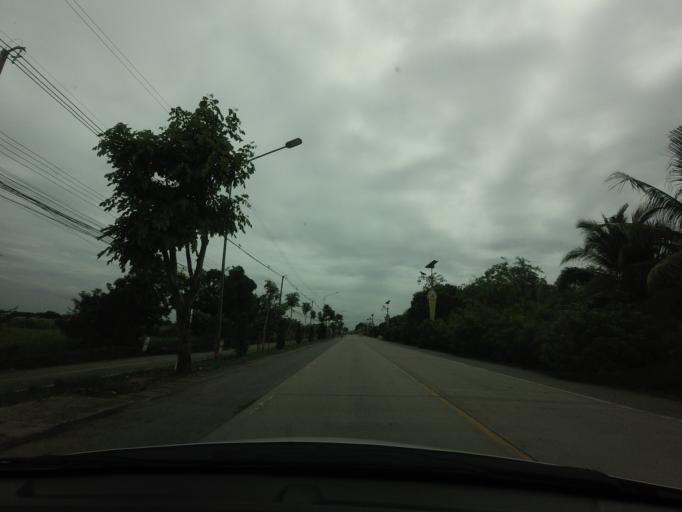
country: TH
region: Pathum Thani
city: Lam Luk Ka
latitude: 13.9306
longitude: 100.7424
